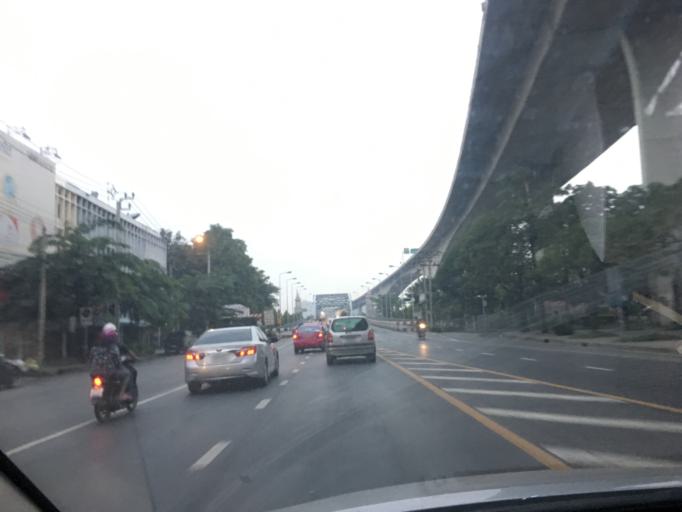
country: TH
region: Bangkok
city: Bang Kho Laem
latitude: 13.6991
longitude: 100.4950
